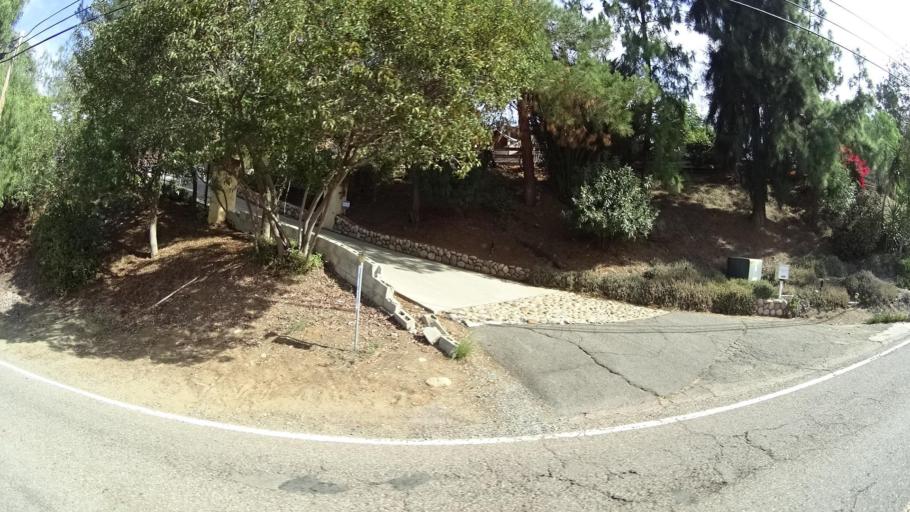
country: US
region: California
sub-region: San Diego County
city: Alpine
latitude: 32.8350
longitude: -116.7931
